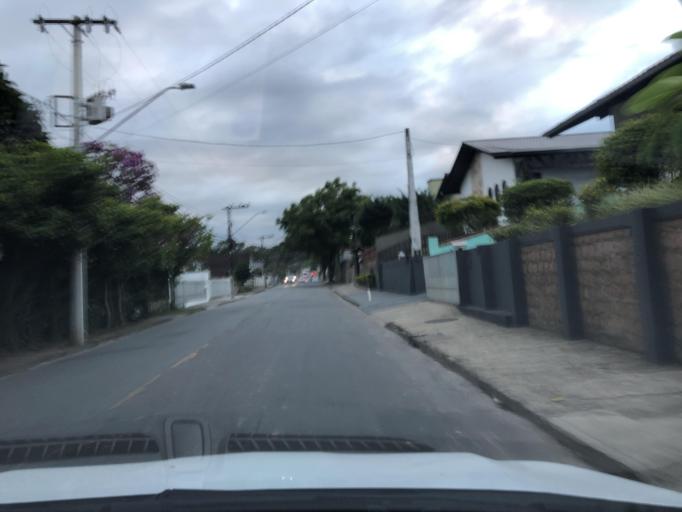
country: BR
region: Santa Catarina
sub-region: Joinville
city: Joinville
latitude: -26.2909
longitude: -48.8742
